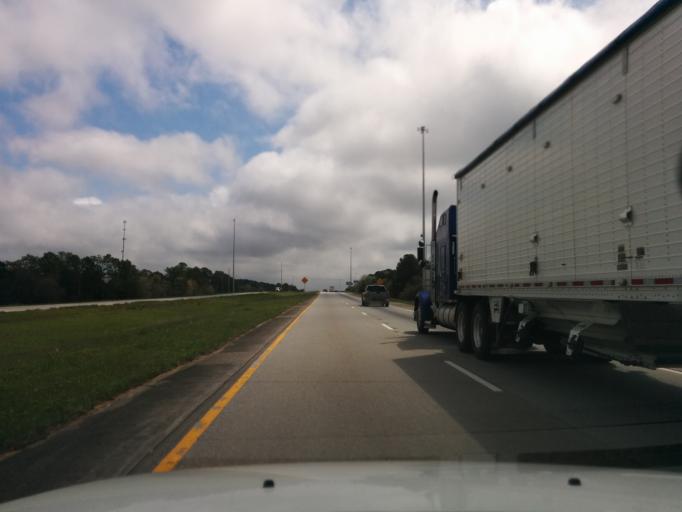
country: US
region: Georgia
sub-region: Emanuel County
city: Swainsboro
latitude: 32.4028
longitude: -82.3107
